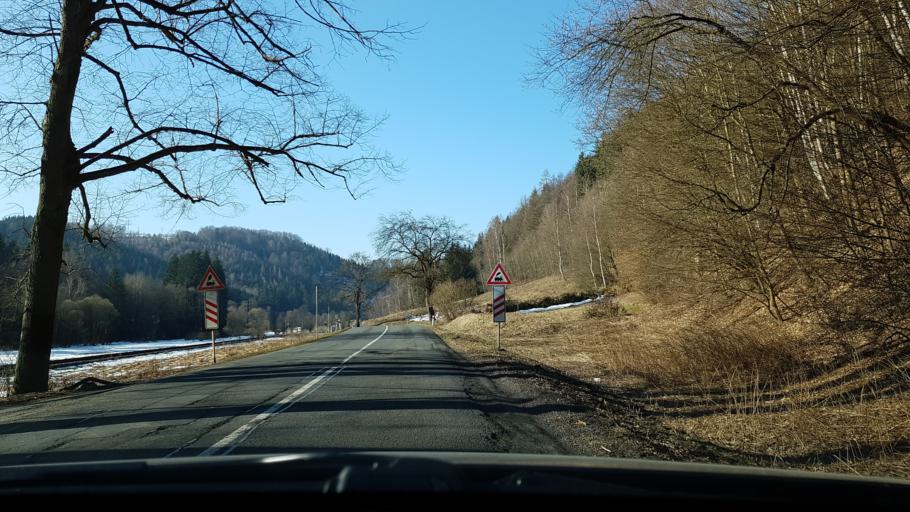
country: CZ
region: Olomoucky
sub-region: Okres Sumperk
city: Hanusovice
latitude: 50.0823
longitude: 16.9680
